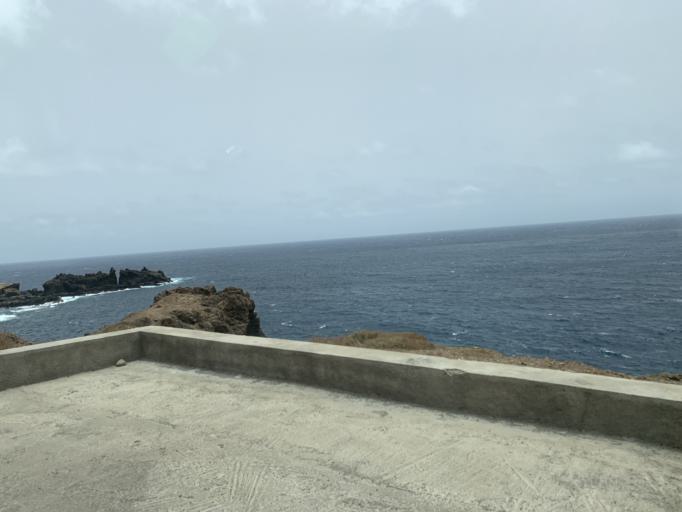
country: CV
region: Brava
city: Vila Nova Sintra
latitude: 14.8666
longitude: -24.7402
